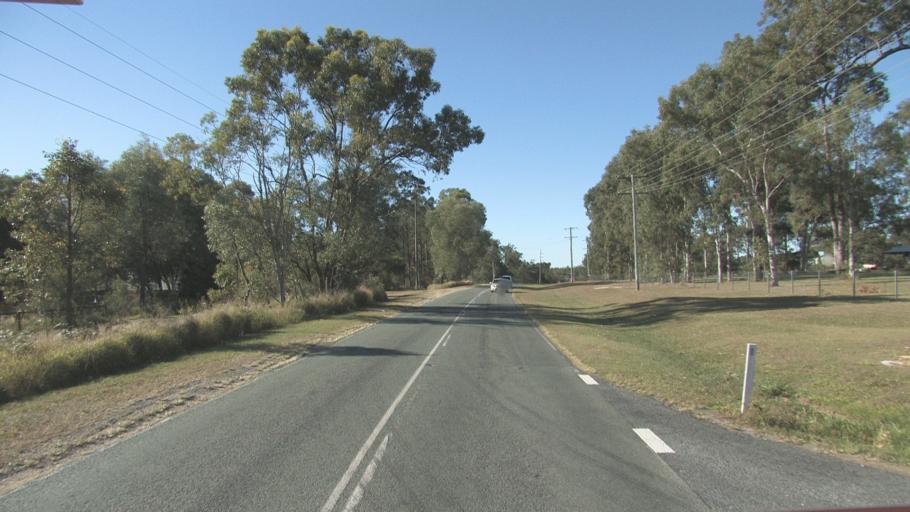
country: AU
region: Queensland
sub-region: Logan
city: North Maclean
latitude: -27.7886
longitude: 153.0439
